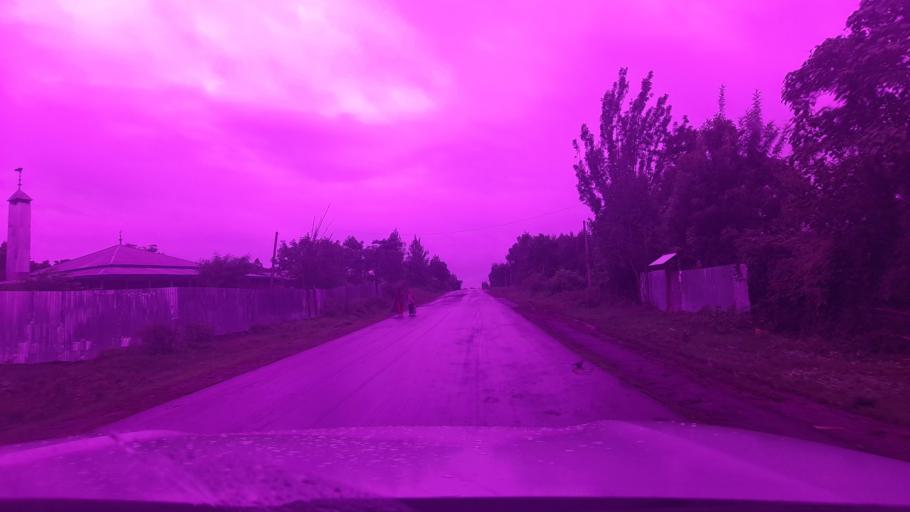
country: ET
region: Oromiya
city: Jima
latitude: 7.8103
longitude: 37.3437
